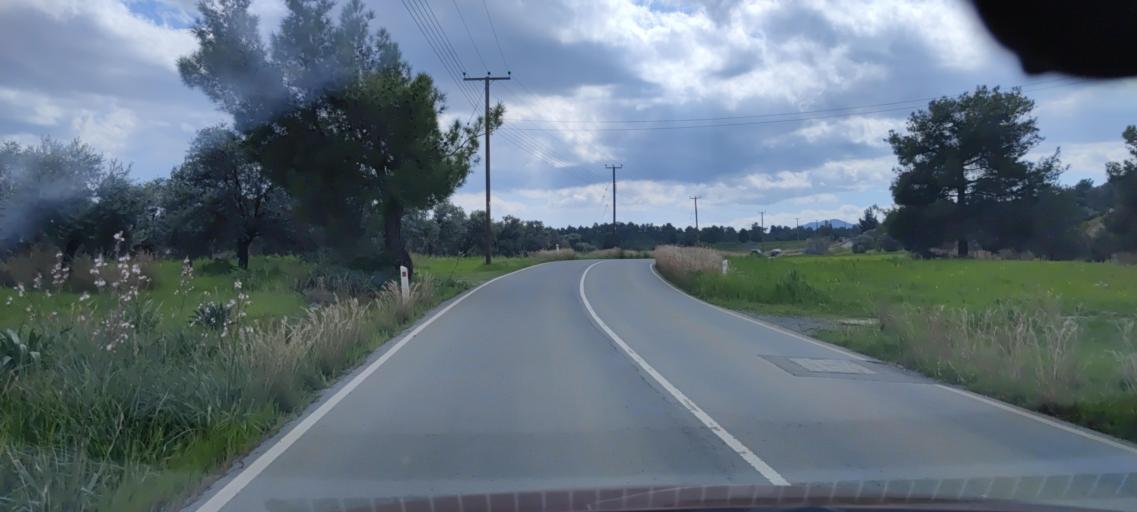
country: CY
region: Lefkosia
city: Lythrodontas
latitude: 34.9765
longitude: 33.2962
